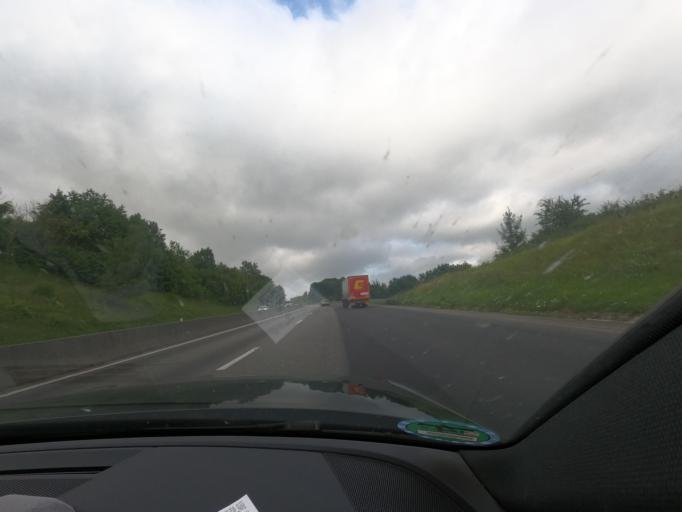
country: FR
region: Haute-Normandie
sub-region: Departement de la Seine-Maritime
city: Neufchatel-en-Bray
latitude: 49.7331
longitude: 1.4654
